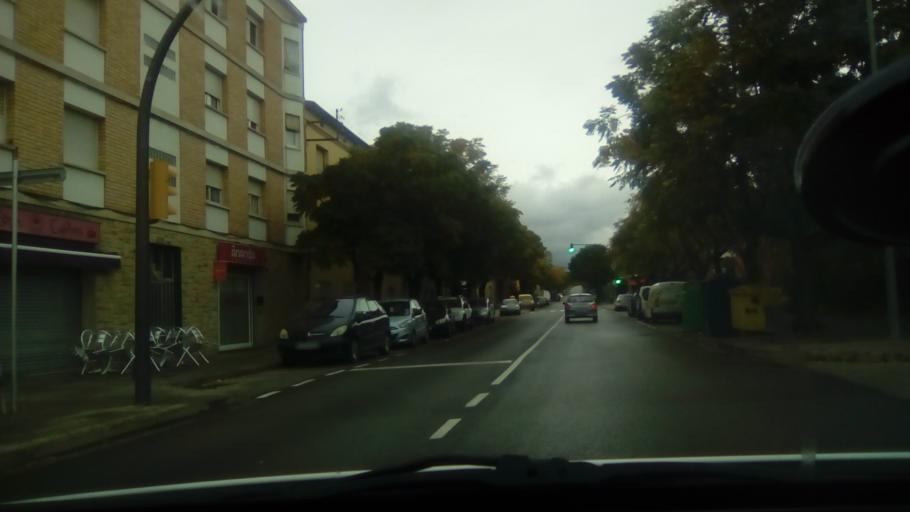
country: ES
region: Catalonia
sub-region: Provincia de Barcelona
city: Monistrol de Montserrat
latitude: 41.6704
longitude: 1.8629
